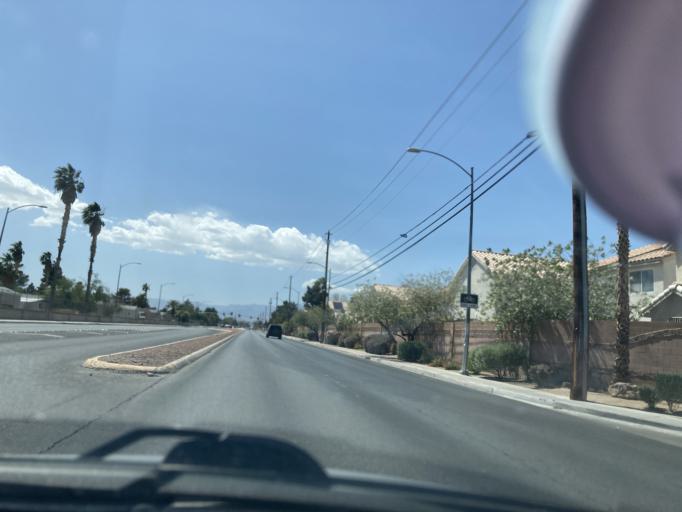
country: US
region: Nevada
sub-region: Clark County
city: Sunrise Manor
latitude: 36.1810
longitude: -115.0860
